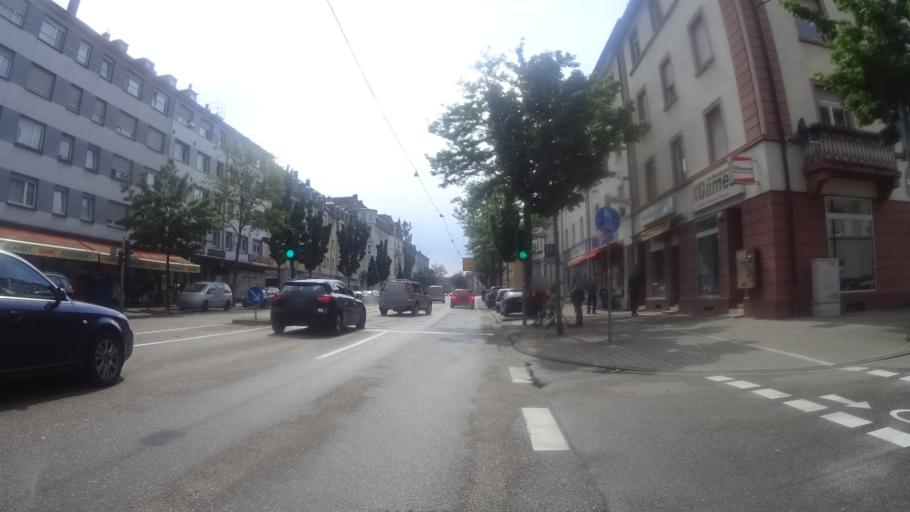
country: DE
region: Baden-Wuerttemberg
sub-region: Karlsruhe Region
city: Rastatt
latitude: 48.8600
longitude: 8.2130
